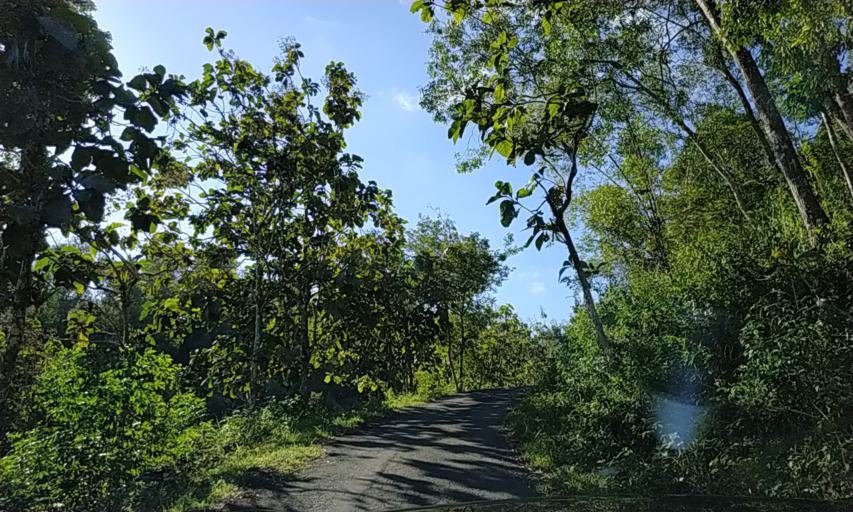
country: ID
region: East Java
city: Krajan
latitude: -8.1311
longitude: 110.9029
